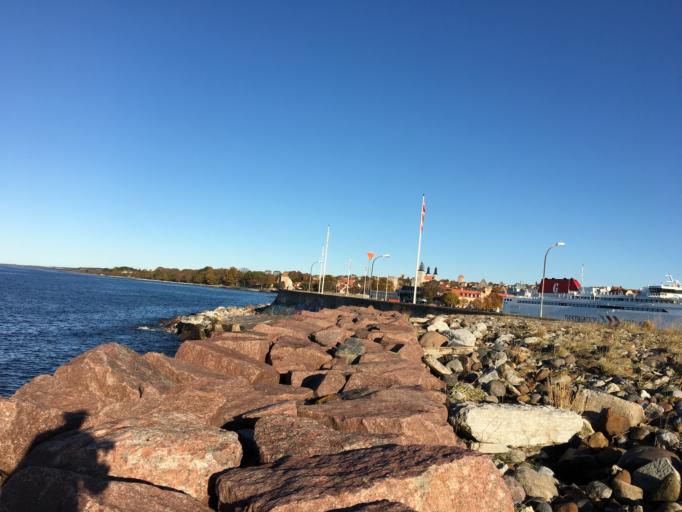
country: SE
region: Gotland
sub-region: Gotland
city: Visby
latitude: 57.6380
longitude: 18.2817
